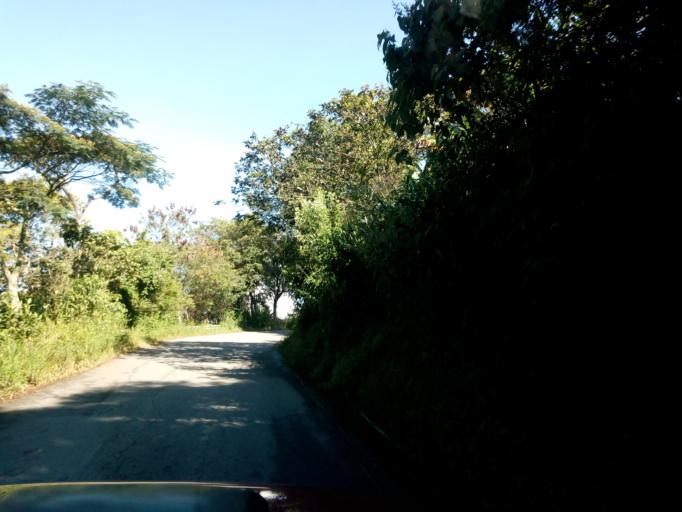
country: CO
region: Boyaca
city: Moniquira
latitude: 5.8755
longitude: -73.5507
